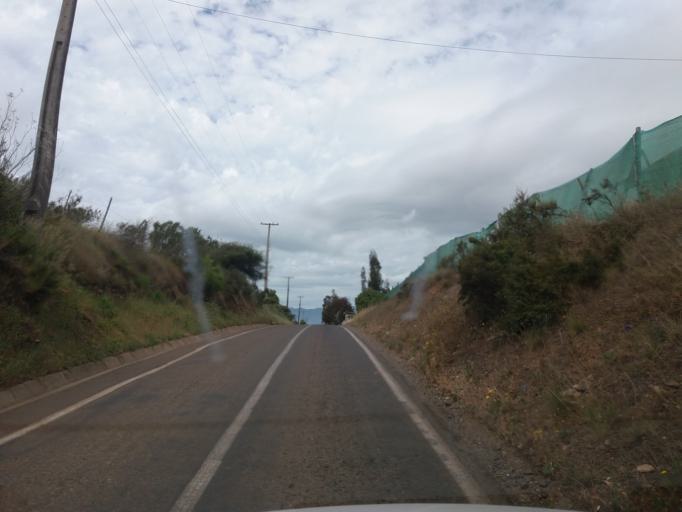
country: CL
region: Valparaiso
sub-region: Provincia de Quillota
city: Quillota
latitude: -32.9169
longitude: -71.3600
